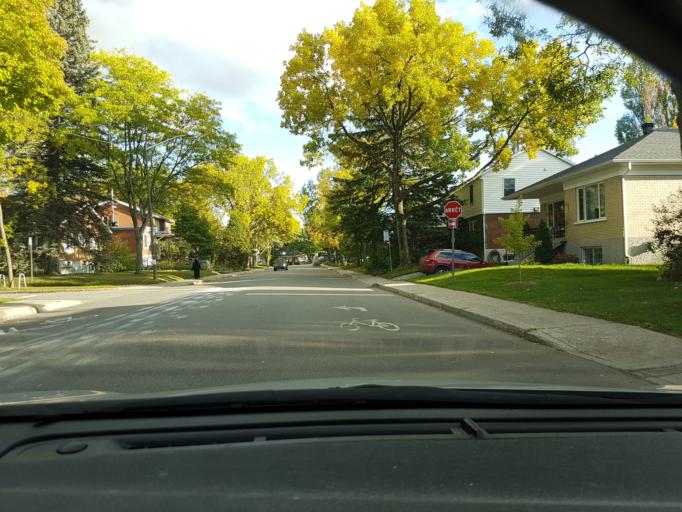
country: CA
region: Quebec
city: Quebec
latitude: 46.7904
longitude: -71.2550
